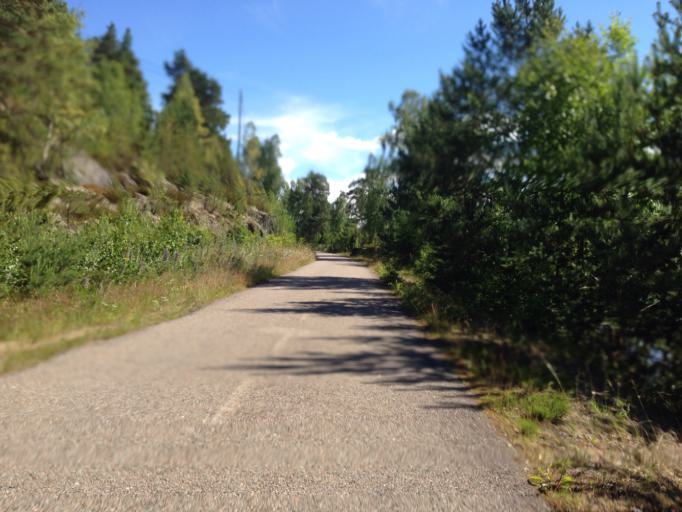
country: SE
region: Dalarna
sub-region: Ludvika Kommun
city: Ludvika
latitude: 60.1657
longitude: 15.1623
